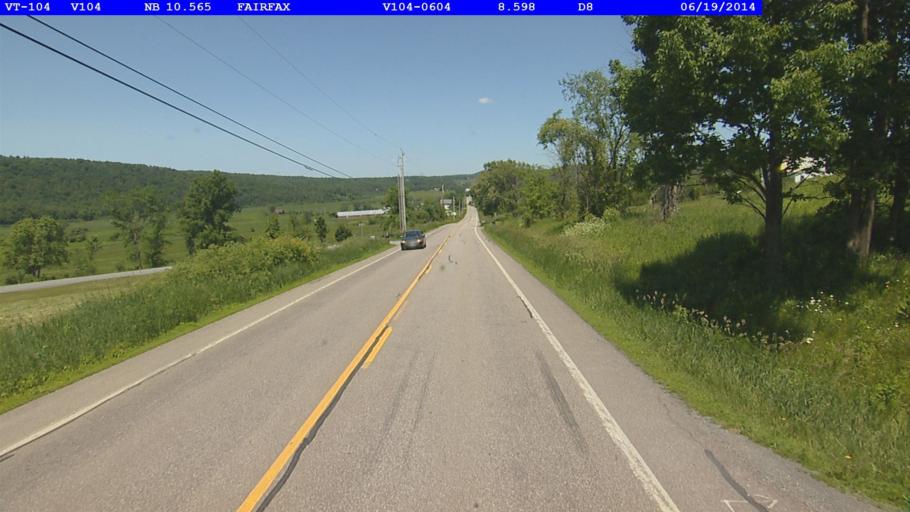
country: US
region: Vermont
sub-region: Chittenden County
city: Milton
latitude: 44.7084
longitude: -73.0371
